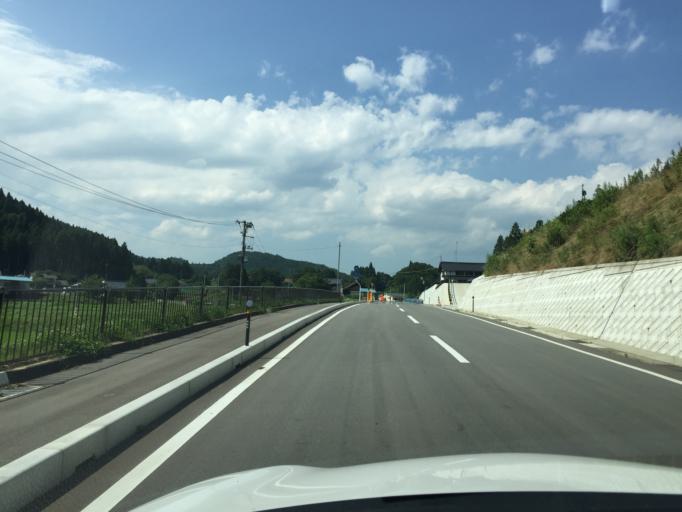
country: JP
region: Ibaraki
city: Kitaibaraki
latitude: 36.9601
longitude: 140.7038
